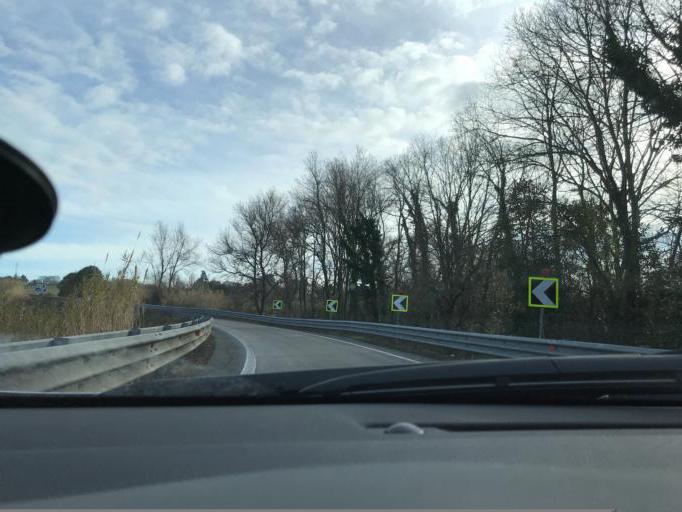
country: IT
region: The Marches
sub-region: Provincia di Ancona
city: Falconara Marittima
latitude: 43.6141
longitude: 13.3846
